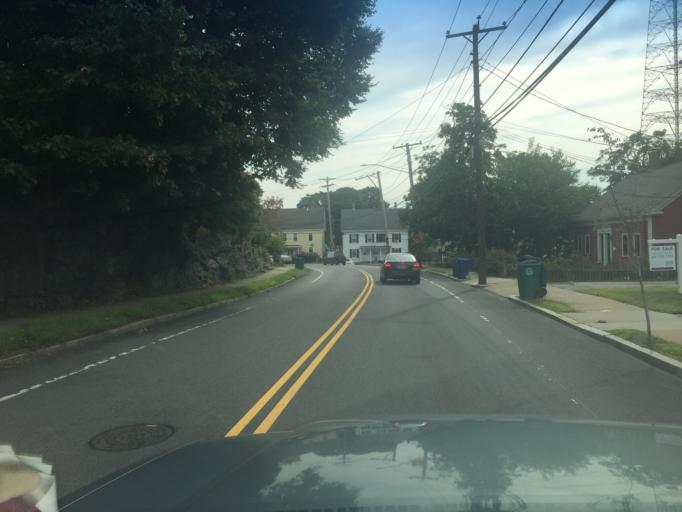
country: US
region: Massachusetts
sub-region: Middlesex County
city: Newton
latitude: 42.3126
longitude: -71.2199
